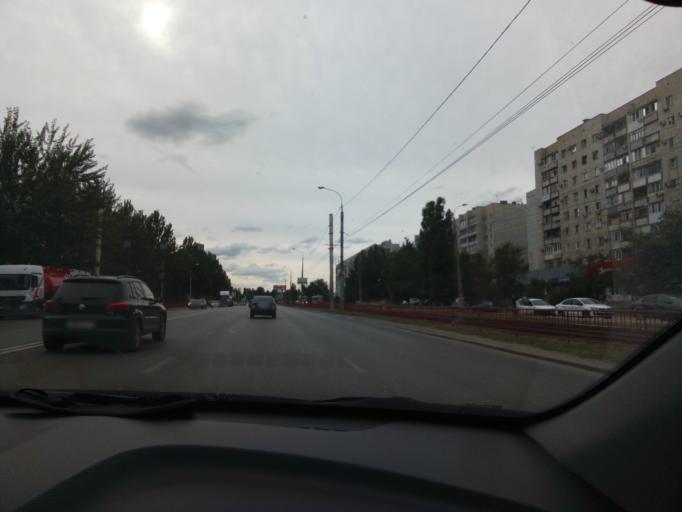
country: RU
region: Volgograd
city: Krasnoslobodsk
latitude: 48.5144
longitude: 44.5408
